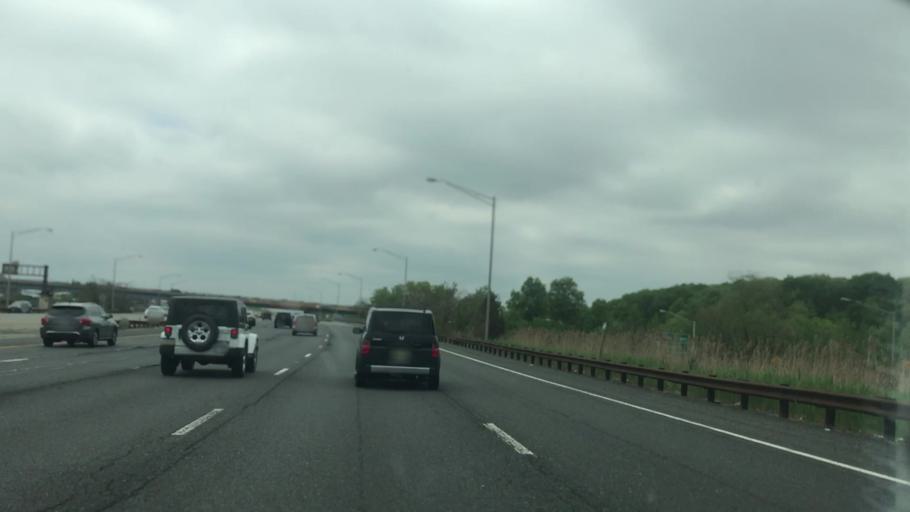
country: US
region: New Jersey
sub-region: Middlesex County
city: Fords
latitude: 40.5225
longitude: -74.3007
